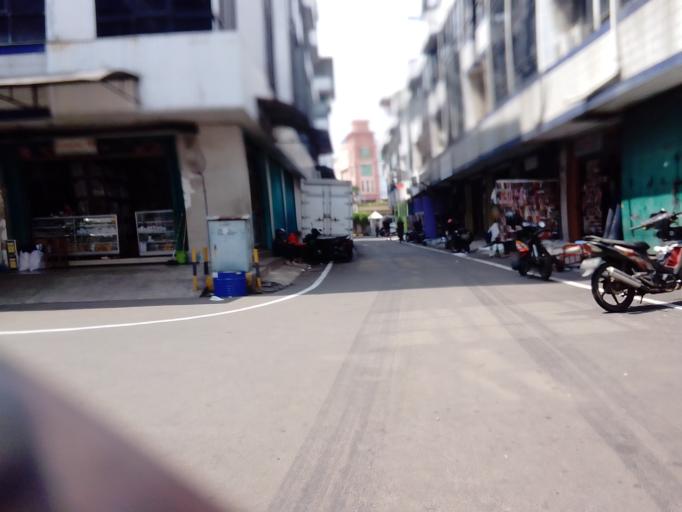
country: ID
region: Jakarta Raya
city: Jakarta
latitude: -6.1367
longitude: 106.8298
